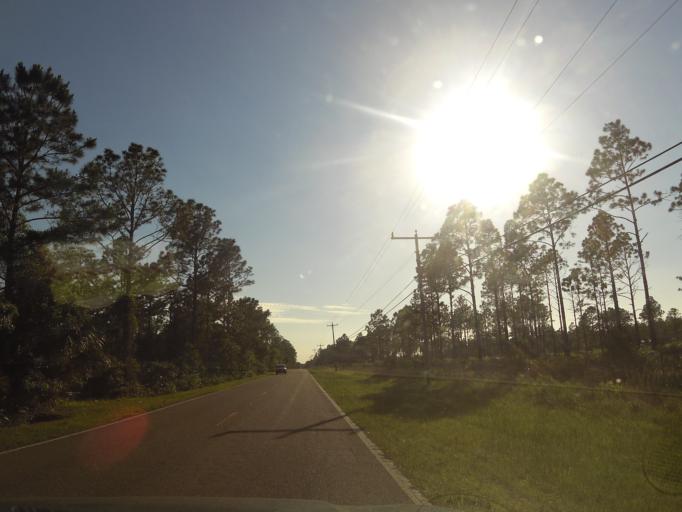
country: US
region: Florida
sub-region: Duval County
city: Atlantic Beach
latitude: 30.4614
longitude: -81.4973
